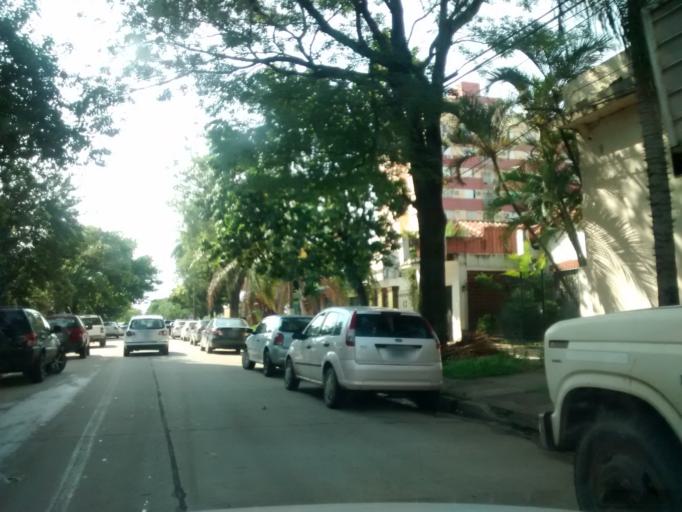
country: AR
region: Chaco
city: Resistencia
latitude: -27.4536
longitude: -58.9769
